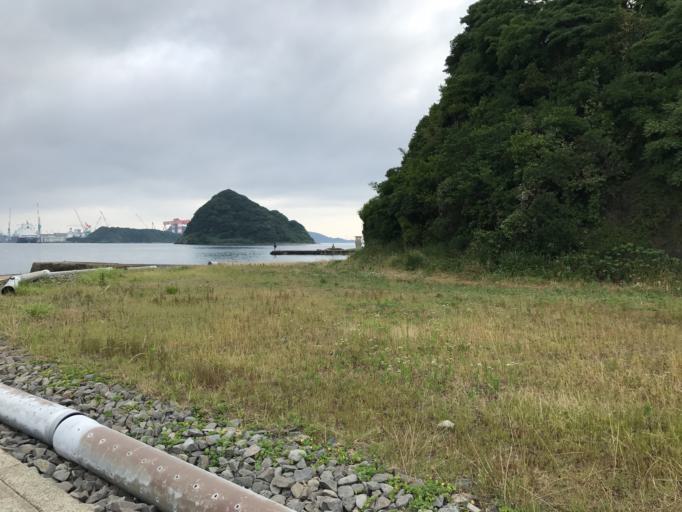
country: JP
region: Nagasaki
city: Nagasaki-shi
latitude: 32.7214
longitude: 129.8373
